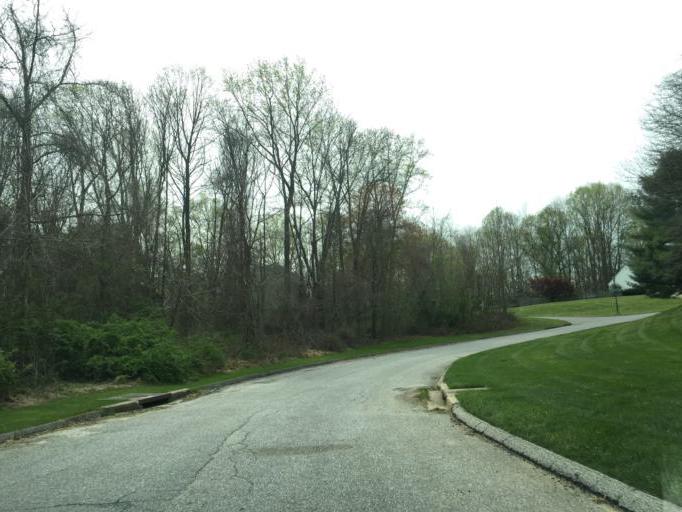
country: US
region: Maryland
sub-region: Baltimore County
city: Hunt Valley
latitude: 39.5572
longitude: -76.6608
